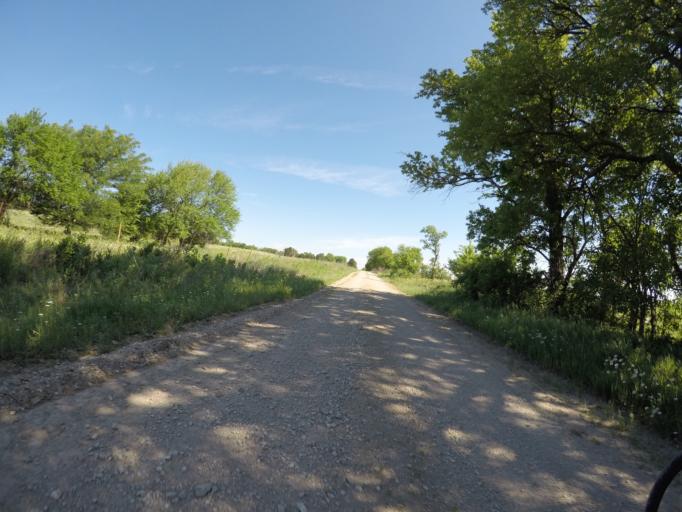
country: US
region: Kansas
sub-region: Wabaunsee County
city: Alma
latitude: 38.9396
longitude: -96.1138
